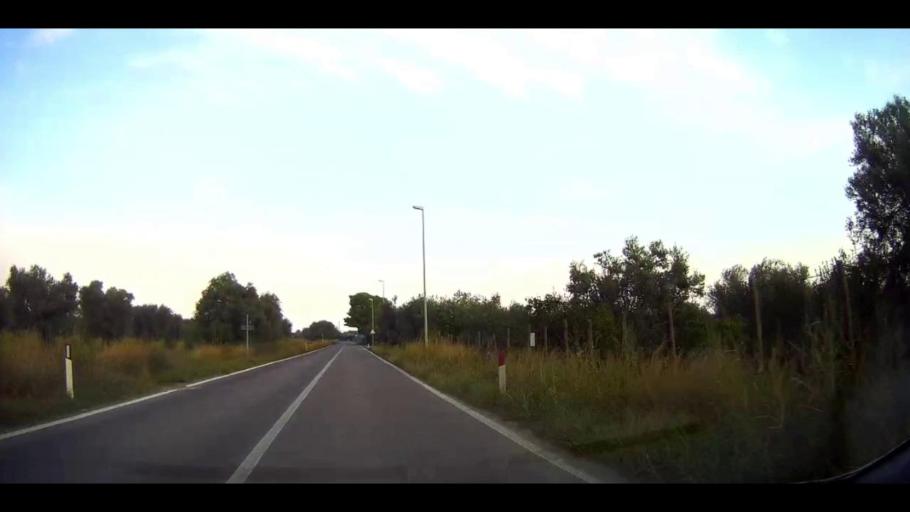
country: IT
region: Calabria
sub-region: Provincia di Crotone
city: Torretta
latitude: 39.4613
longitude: 17.0287
